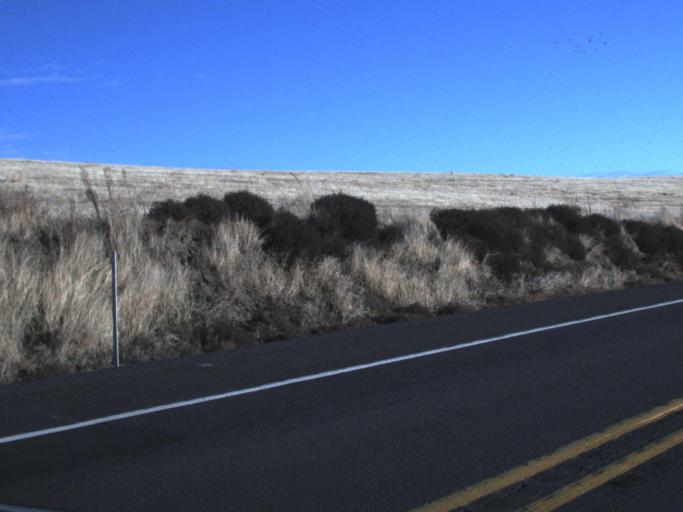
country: US
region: Washington
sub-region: Garfield County
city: Pomeroy
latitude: 46.7145
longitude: -117.7763
